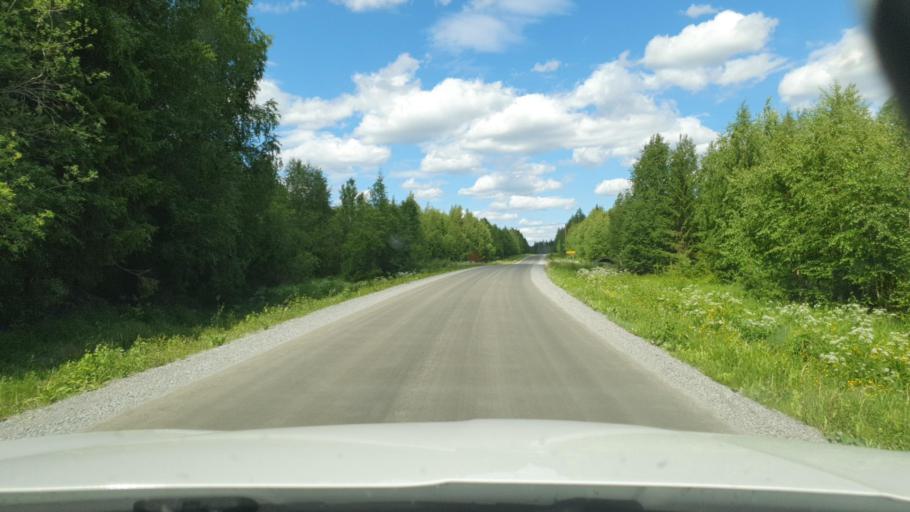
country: SE
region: Vaesterbotten
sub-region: Skelleftea Kommun
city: Forsbacka
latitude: 64.8155
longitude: 20.4932
